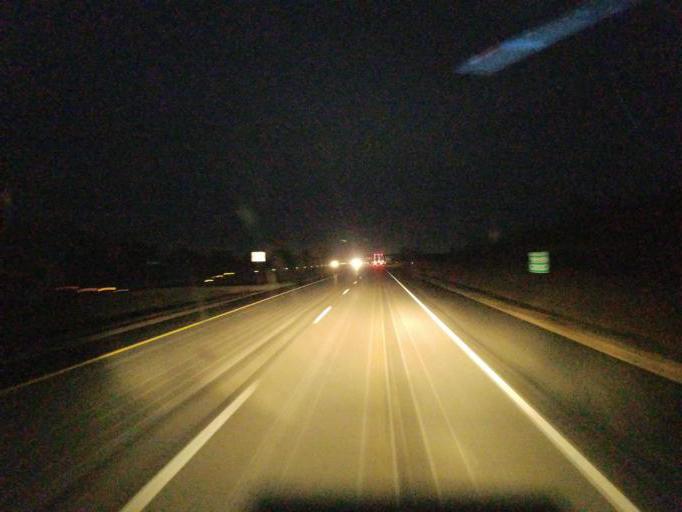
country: US
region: Iowa
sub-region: Guthrie County
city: Stuart
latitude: 41.4959
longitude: -94.3810
